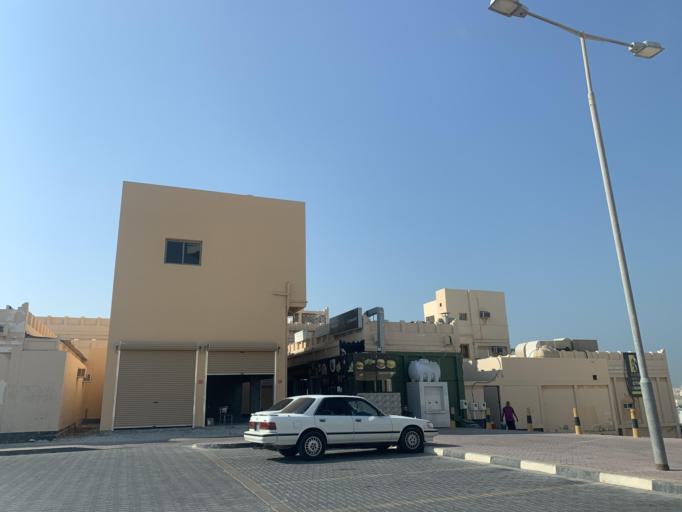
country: BH
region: Central Governorate
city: Madinat Hamad
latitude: 26.1002
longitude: 50.5036
